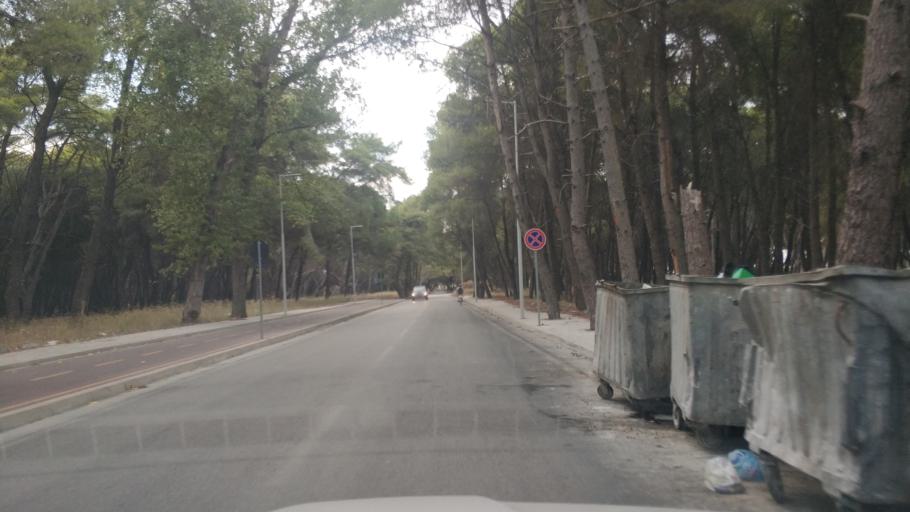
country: AL
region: Vlore
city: Vlore
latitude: 40.4666
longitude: 19.4617
